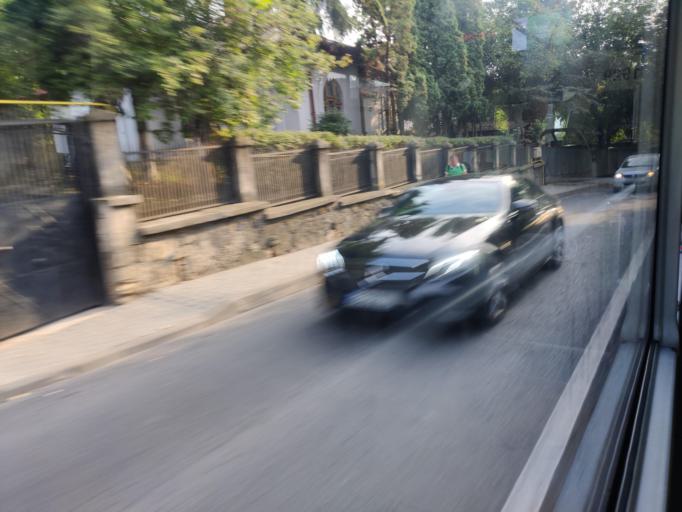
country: RO
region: Iasi
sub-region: Municipiul Iasi
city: Iasi
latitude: 47.1663
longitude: 27.5977
